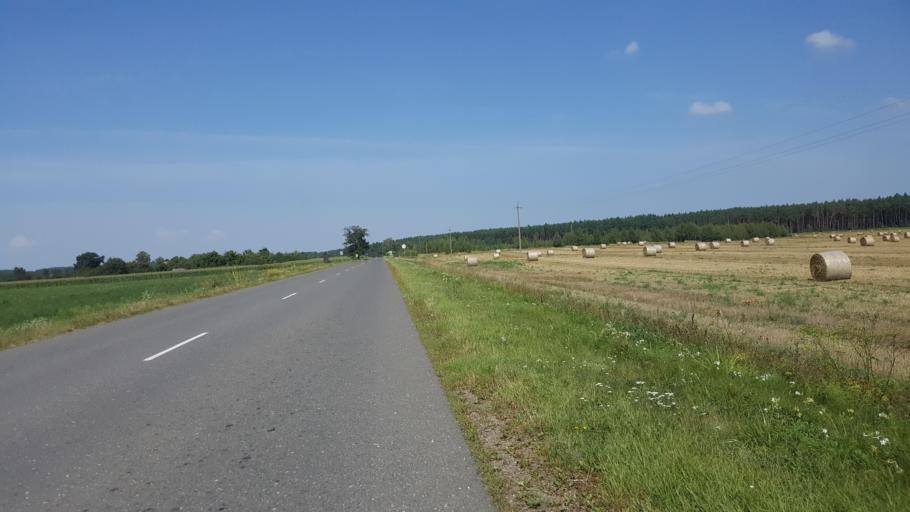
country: BY
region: Brest
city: Kamyanyuki
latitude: 52.4986
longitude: 23.6708
